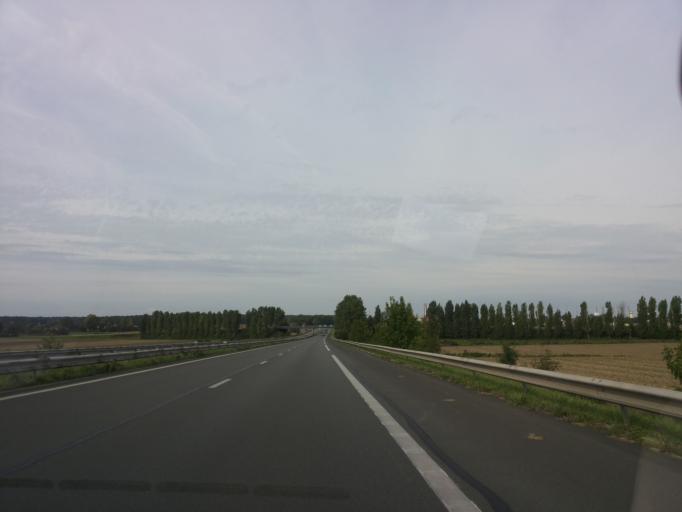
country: FR
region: Nord-Pas-de-Calais
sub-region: Departement du Pas-de-Calais
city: Gosnay
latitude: 50.5195
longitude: 2.5798
